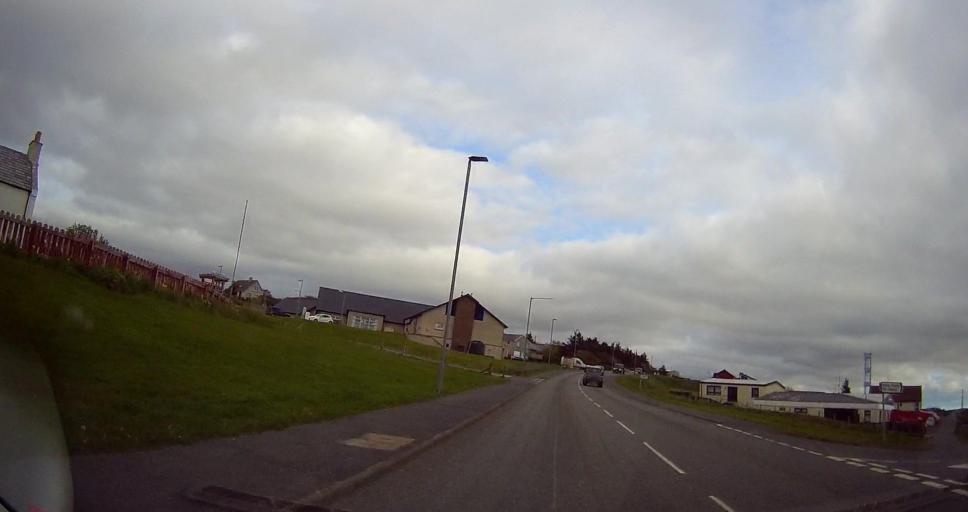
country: GB
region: Scotland
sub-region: Shetland Islands
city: Lerwick
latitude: 60.3952
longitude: -1.3523
